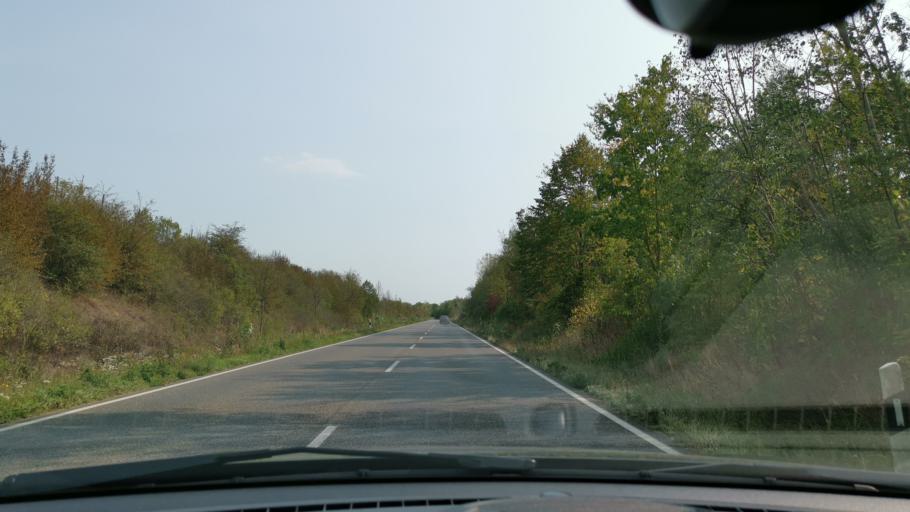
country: DE
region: North Rhine-Westphalia
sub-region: Regierungsbezirk Koln
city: Bedburg
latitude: 50.9755
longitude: 6.5995
